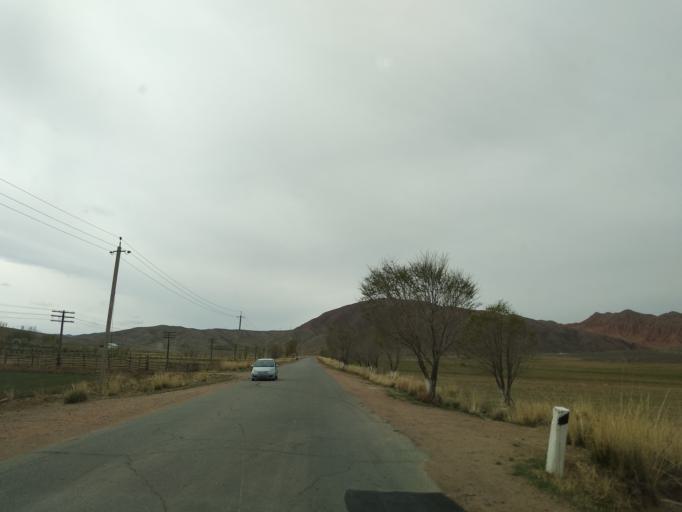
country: KG
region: Ysyk-Koel
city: Bokombayevskoye
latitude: 42.1380
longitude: 76.8227
